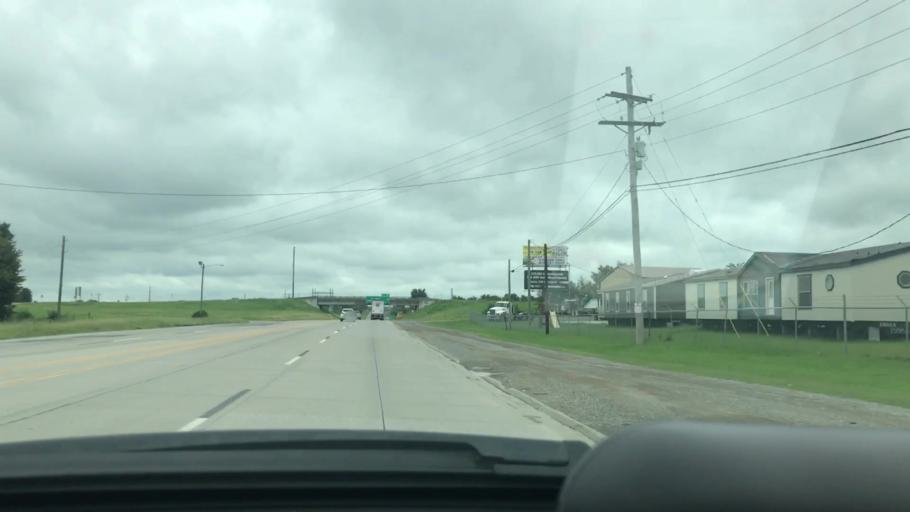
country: US
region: Oklahoma
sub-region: Pittsburg County
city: McAlester
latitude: 34.8337
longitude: -95.8387
